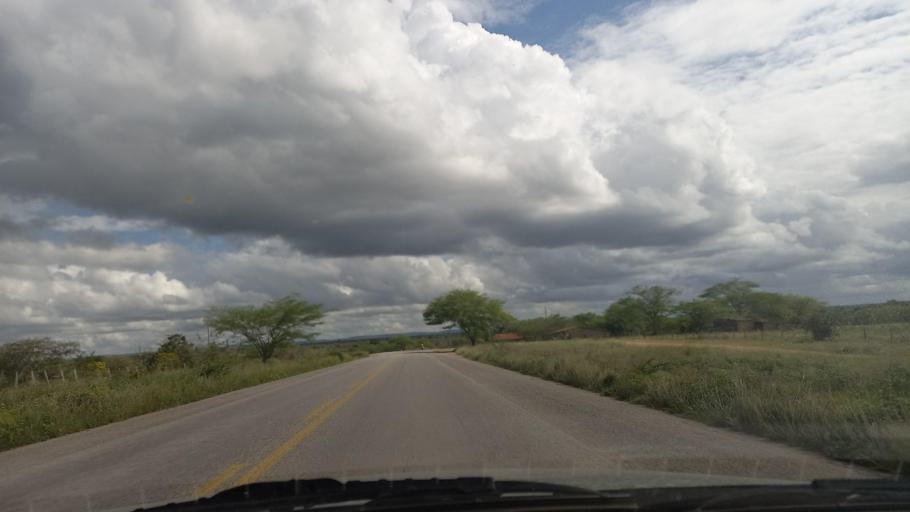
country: BR
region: Pernambuco
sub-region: Cachoeirinha
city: Cachoeirinha
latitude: -8.5007
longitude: -36.2455
